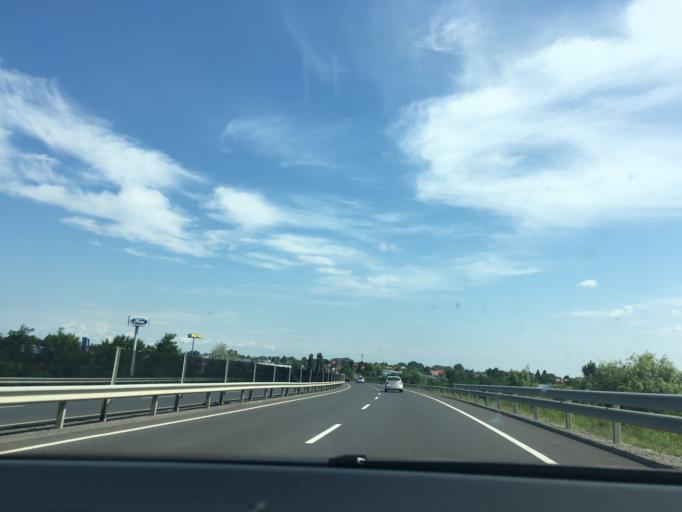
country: HU
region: Szabolcs-Szatmar-Bereg
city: Nyiregyhaza
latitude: 47.9150
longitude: 21.7186
